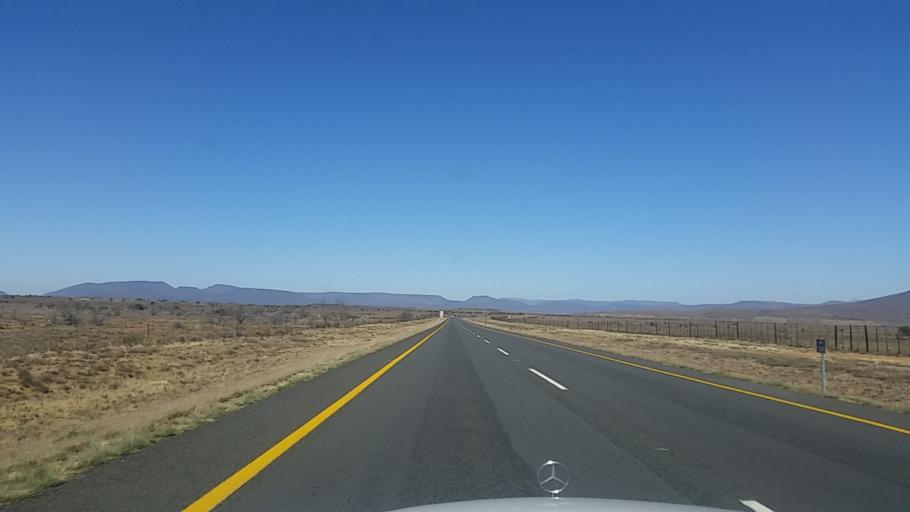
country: ZA
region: Eastern Cape
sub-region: Cacadu District Municipality
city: Graaff-Reinet
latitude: -32.1279
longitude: 24.5921
